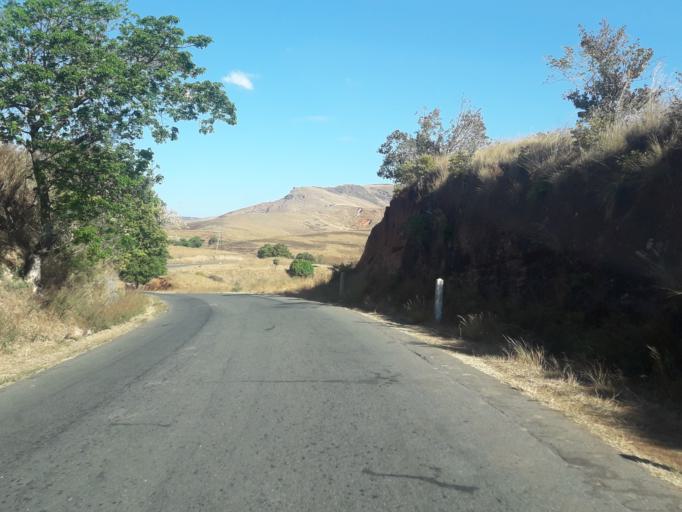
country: MG
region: Betsiboka
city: Maevatanana
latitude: -17.6203
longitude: 46.9436
